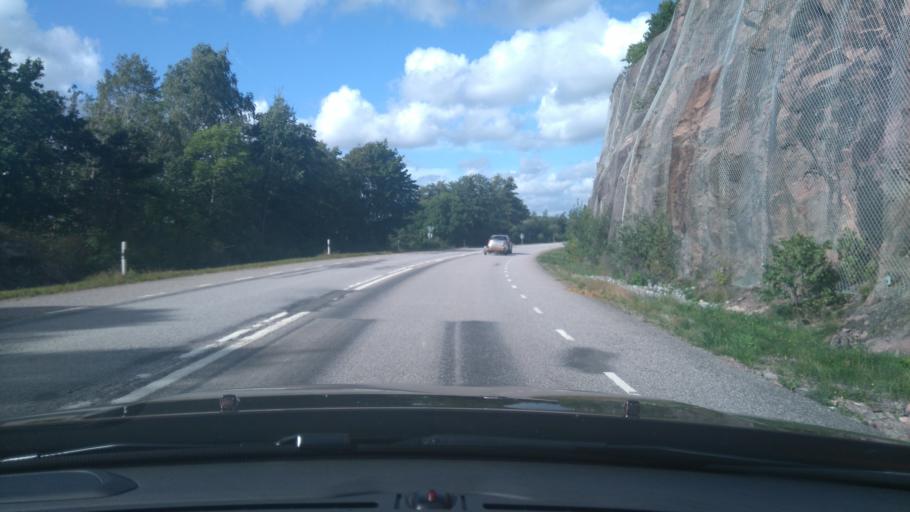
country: SE
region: Vaestra Goetaland
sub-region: Lilla Edets Kommun
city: Lodose
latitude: 58.0395
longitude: 12.1507
